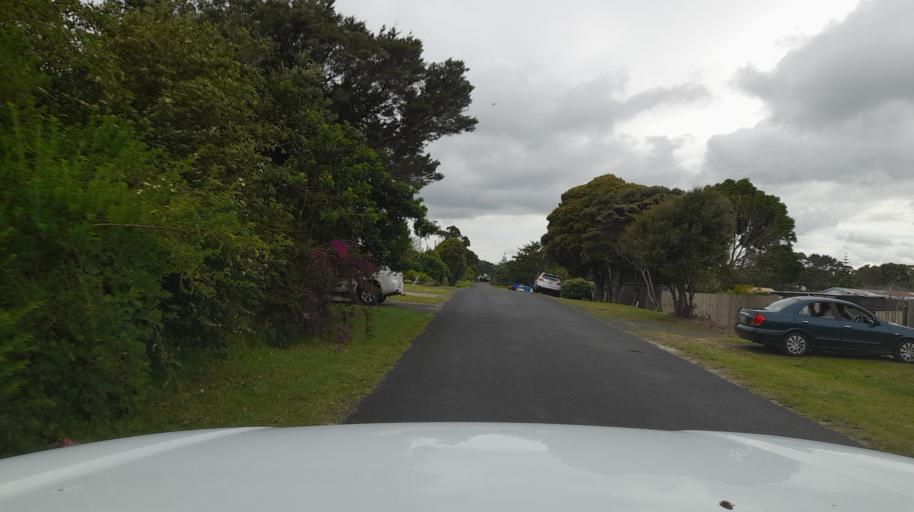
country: NZ
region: Northland
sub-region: Far North District
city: Ahipara
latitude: -35.1636
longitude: 173.1566
